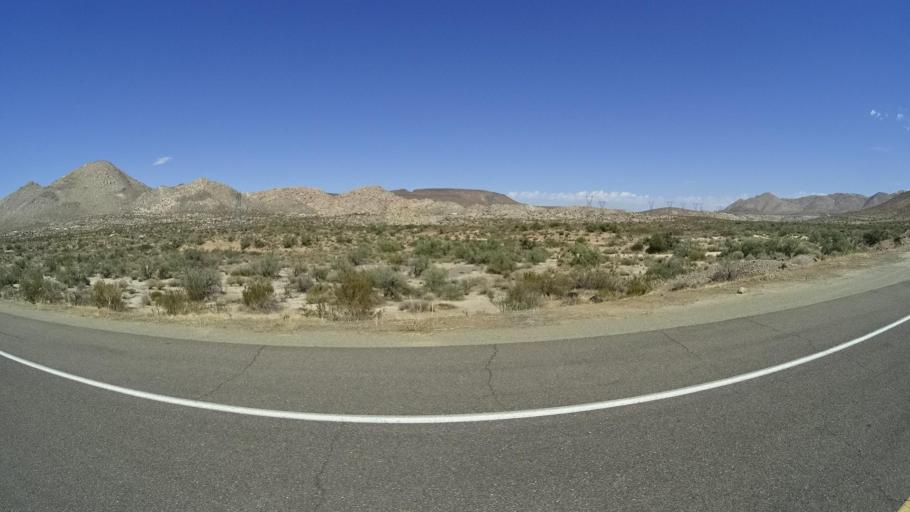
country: MX
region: Baja California
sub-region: Tecate
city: Cereso del Hongo
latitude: 32.6259
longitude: -116.1607
